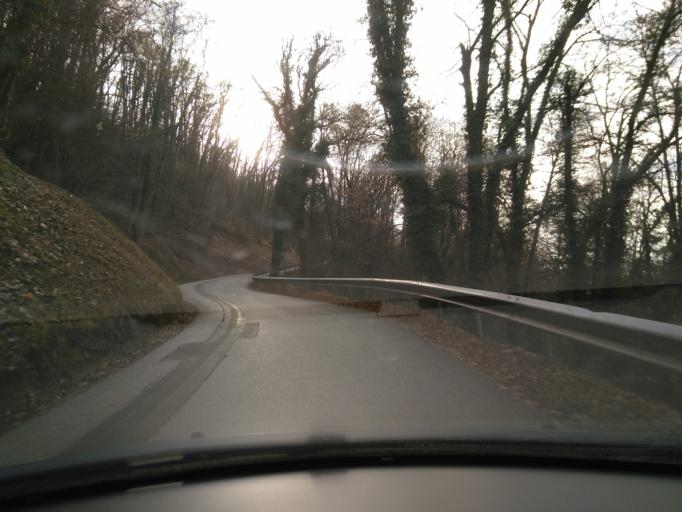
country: FR
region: Rhone-Alpes
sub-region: Departement de l'Isere
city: Villard-Bonnot
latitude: 45.2516
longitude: 5.9064
